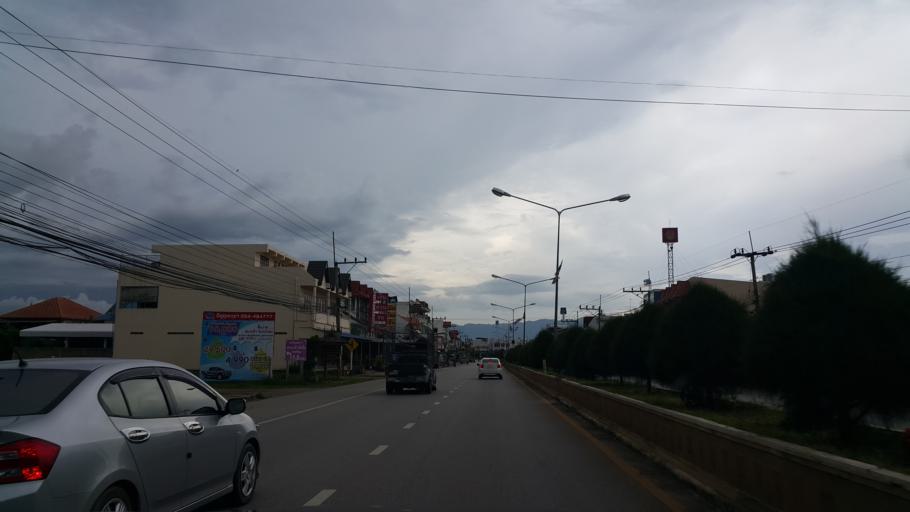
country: TH
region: Phayao
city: Dok Kham Tai
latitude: 19.1621
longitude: 99.9858
